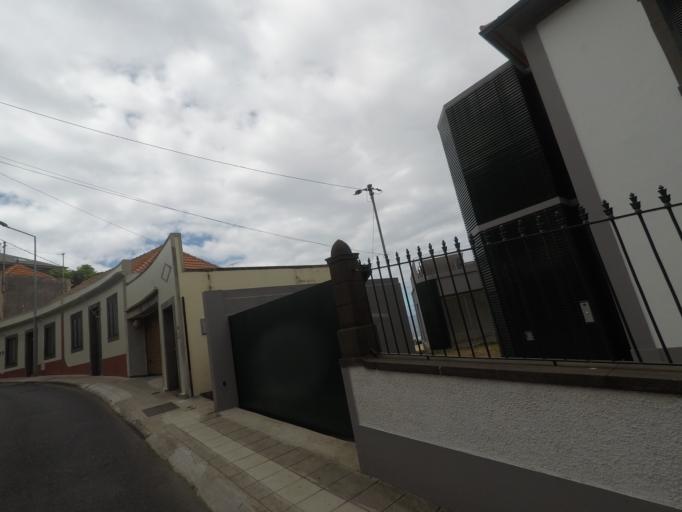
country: PT
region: Madeira
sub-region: Funchal
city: Nossa Senhora do Monte
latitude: 32.6515
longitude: -16.8981
